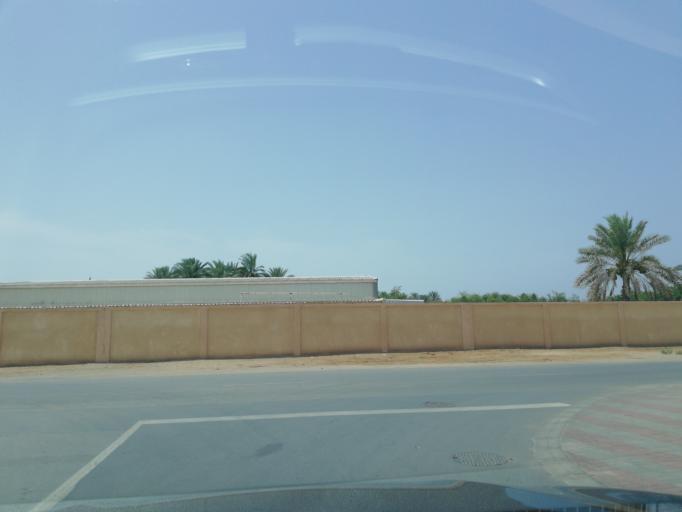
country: OM
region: Muhafazat Masqat
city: As Sib al Jadidah
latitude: 23.6274
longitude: 58.2500
